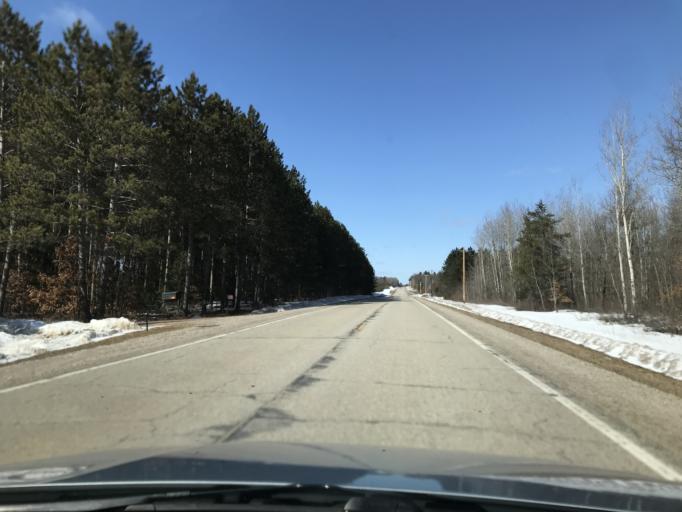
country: US
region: Wisconsin
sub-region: Marinette County
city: Niagara
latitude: 45.3450
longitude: -88.1014
